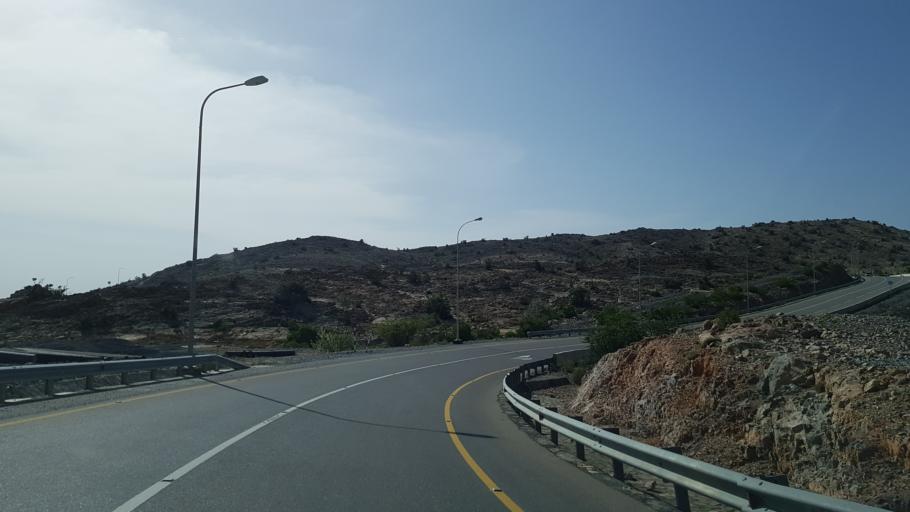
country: OM
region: Muhafazat ad Dakhiliyah
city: Izki
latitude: 23.0423
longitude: 57.7127
